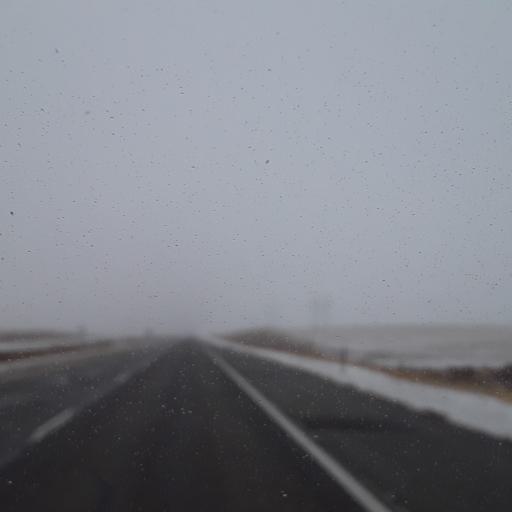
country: US
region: Nebraska
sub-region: Cheyenne County
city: Sidney
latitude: 40.7977
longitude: -102.8738
